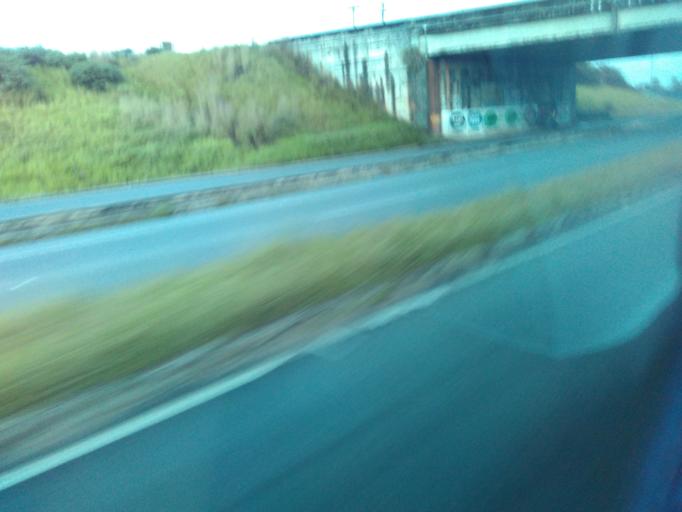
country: BR
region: Sergipe
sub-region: Nossa Senhora Do Socorro
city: Nossa Senhora do Socorro
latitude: -10.9033
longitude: -37.1302
